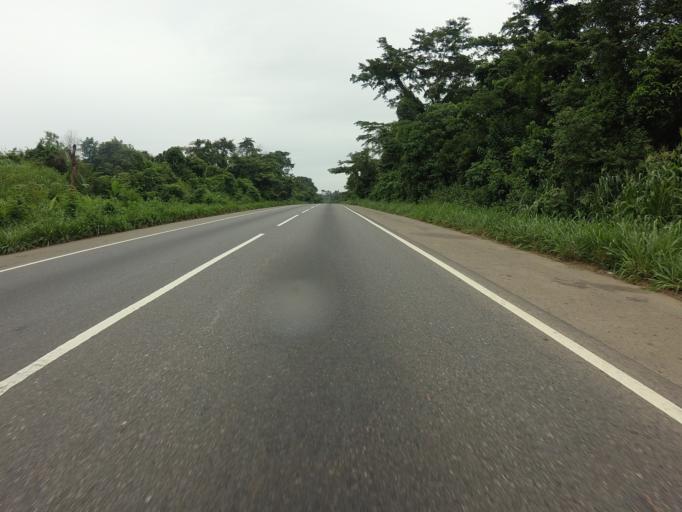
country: GH
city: Kibi
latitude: 6.1875
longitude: -0.4693
